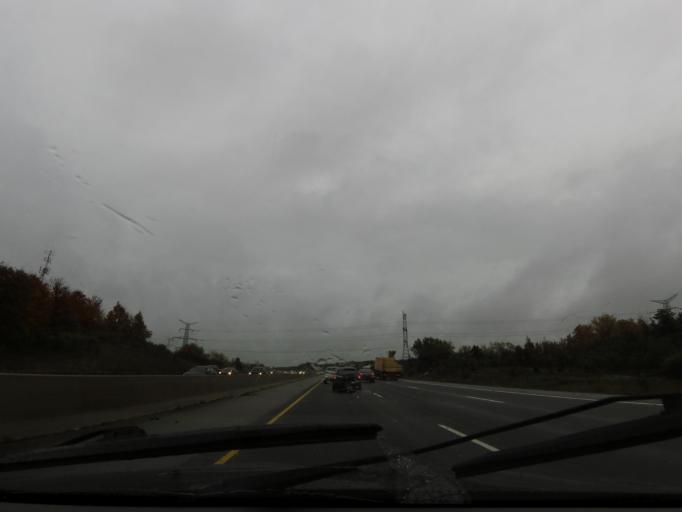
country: CA
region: Ontario
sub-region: Wellington County
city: Guelph
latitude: 43.4495
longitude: -80.1413
